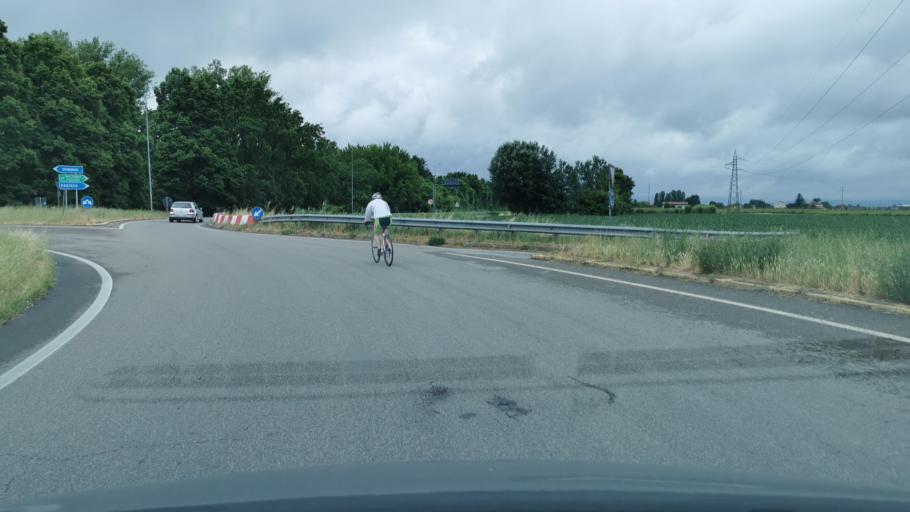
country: IT
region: Emilia-Romagna
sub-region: Provincia di Ravenna
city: Granarolo
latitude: 44.3617
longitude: 11.9327
